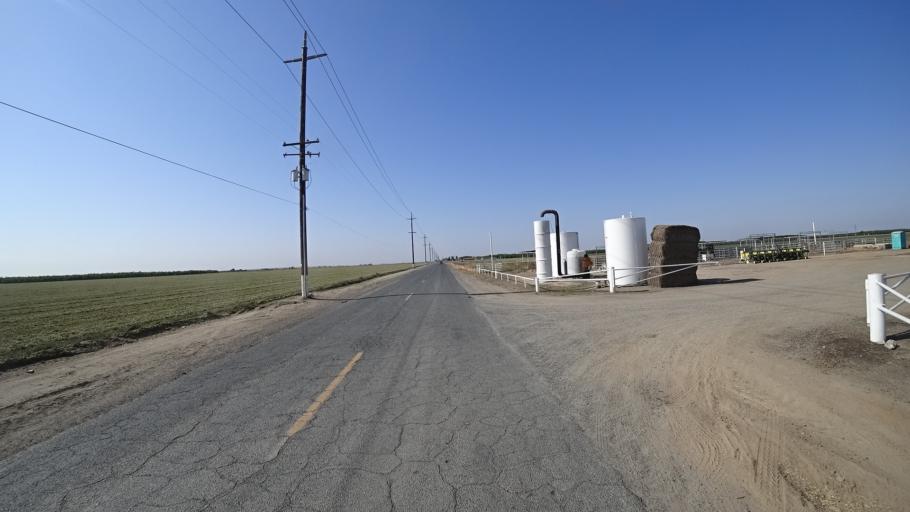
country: US
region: California
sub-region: Kings County
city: Home Garden
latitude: 36.2682
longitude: -119.5831
